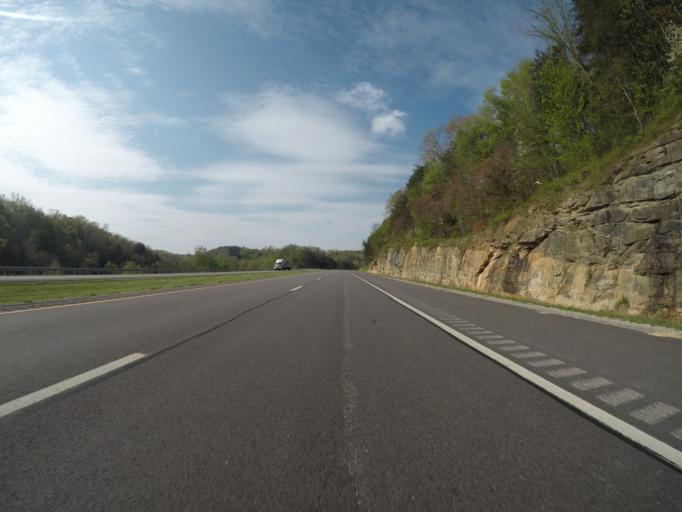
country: US
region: West Virginia
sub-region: Kanawha County
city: Alum Creek
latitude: 38.2851
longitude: -81.7647
